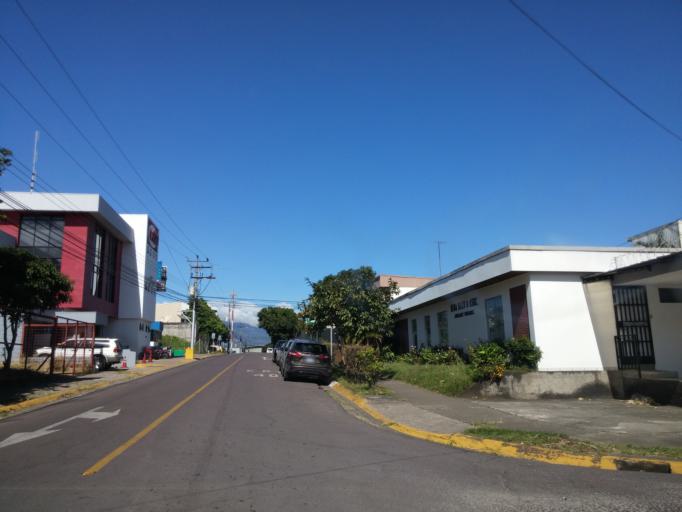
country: CR
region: San Jose
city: Colima
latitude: 9.9463
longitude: -84.1049
